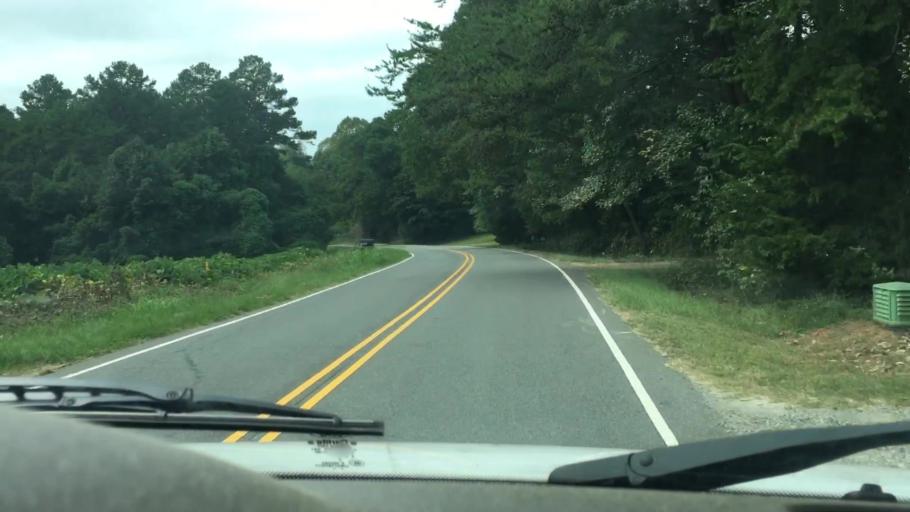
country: US
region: North Carolina
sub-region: Gaston County
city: Davidson
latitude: 35.5061
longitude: -80.8052
